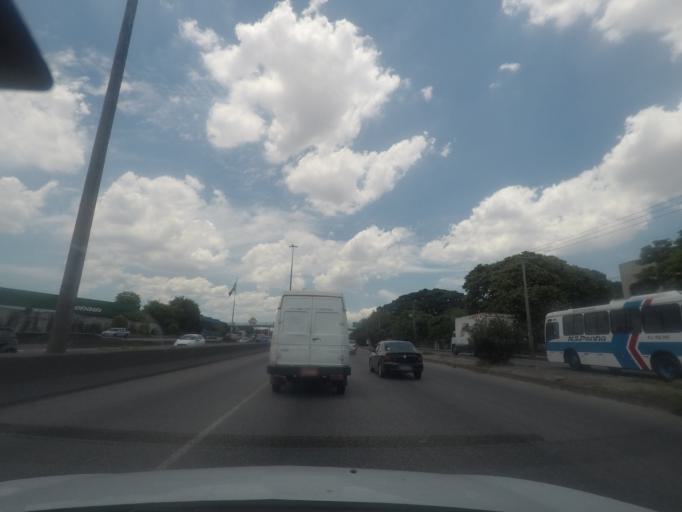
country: BR
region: Rio de Janeiro
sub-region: Sao Joao De Meriti
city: Sao Joao de Meriti
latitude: -22.8258
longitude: -43.3372
